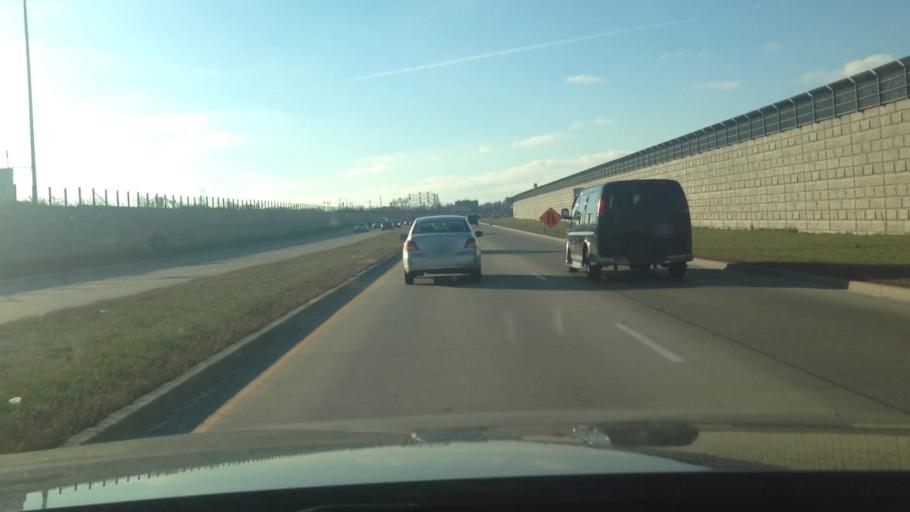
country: US
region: Illinois
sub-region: DuPage County
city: Bensenville
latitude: 41.9553
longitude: -87.9244
